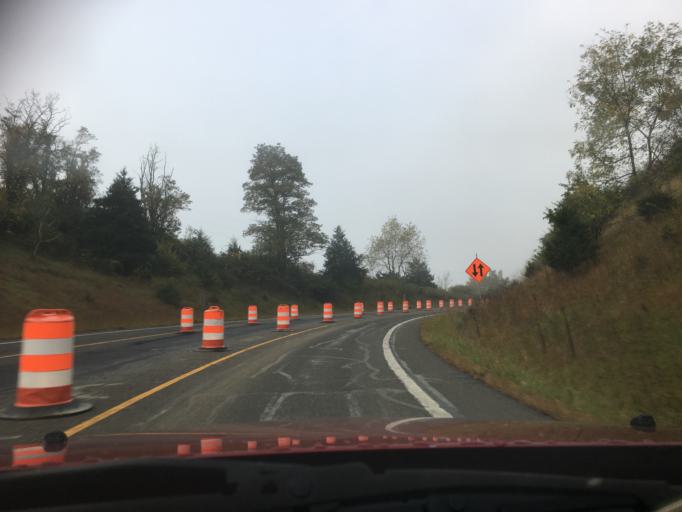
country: US
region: Virginia
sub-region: City of Radford
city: Radford
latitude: 37.0900
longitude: -80.5735
